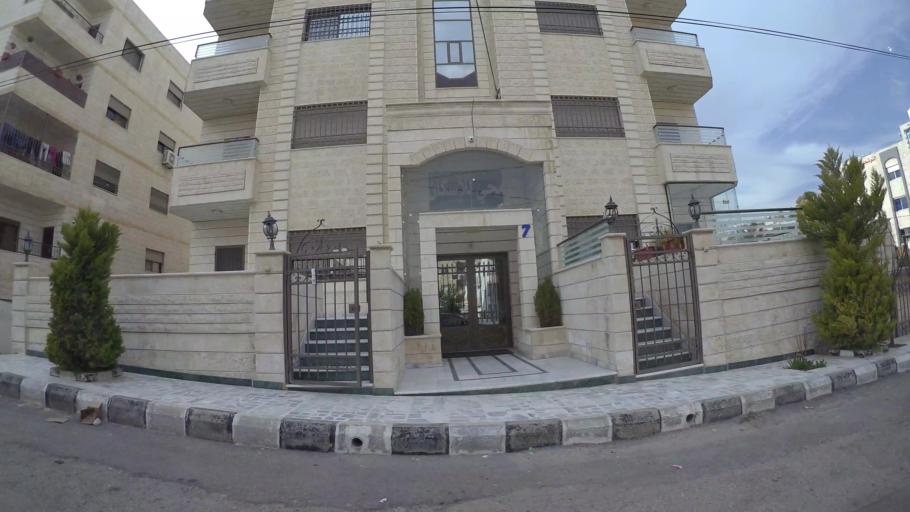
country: JO
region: Amman
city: Amman
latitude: 32.0010
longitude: 35.9491
